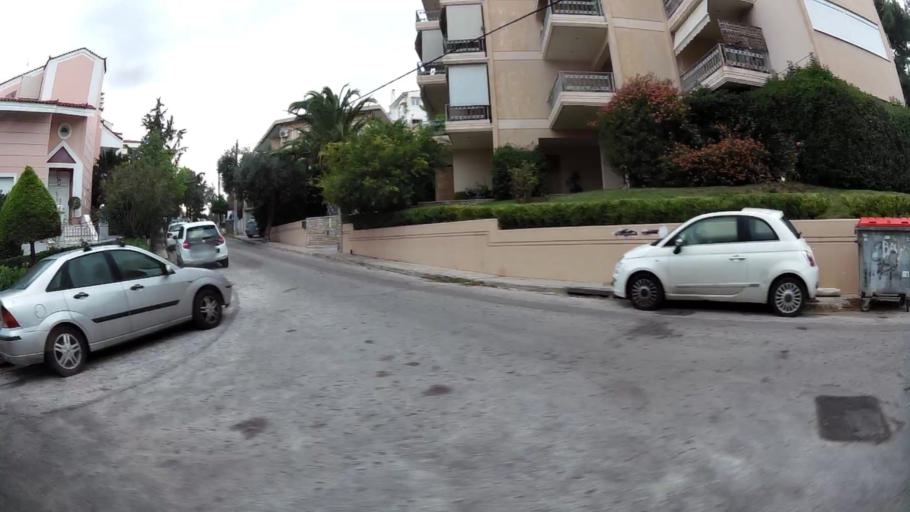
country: GR
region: Attica
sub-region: Nomarchia Athinas
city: Melissia
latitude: 38.0488
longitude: 23.8375
